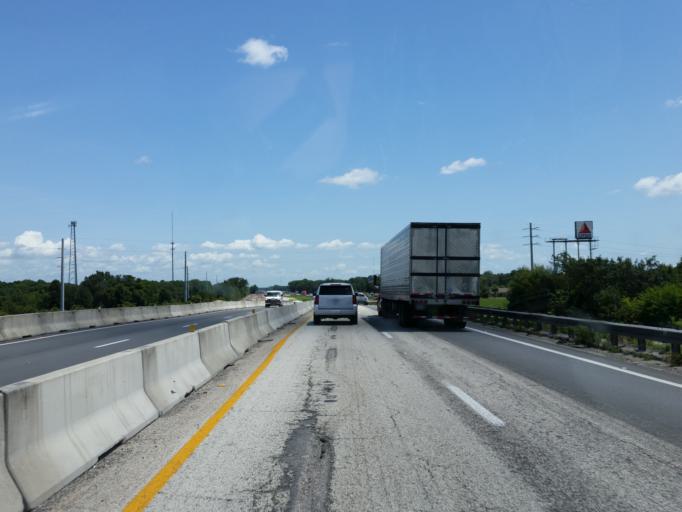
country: US
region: Florida
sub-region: Sumter County
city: Bushnell
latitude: 28.6689
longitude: -82.1425
